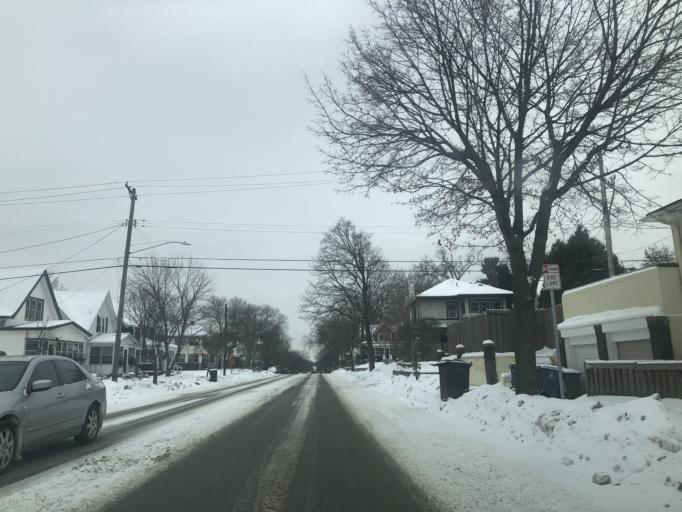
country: US
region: Minnesota
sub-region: Hennepin County
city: Richfield
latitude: 44.9304
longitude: -93.2842
